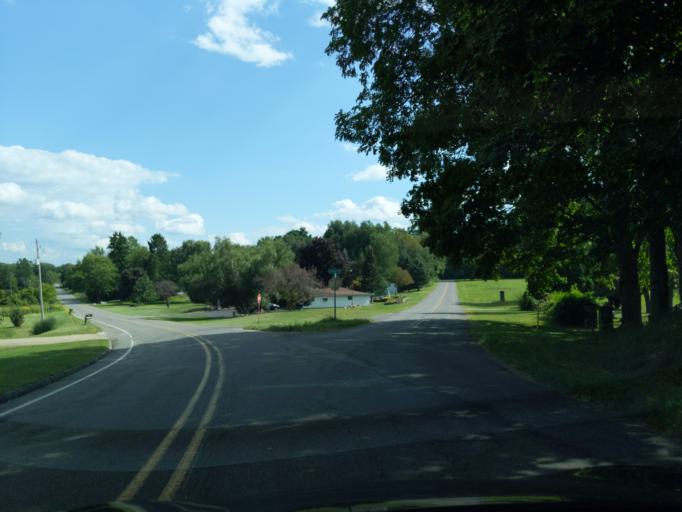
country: US
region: Michigan
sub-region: Jackson County
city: Spring Arbor
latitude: 42.3095
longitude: -84.5180
